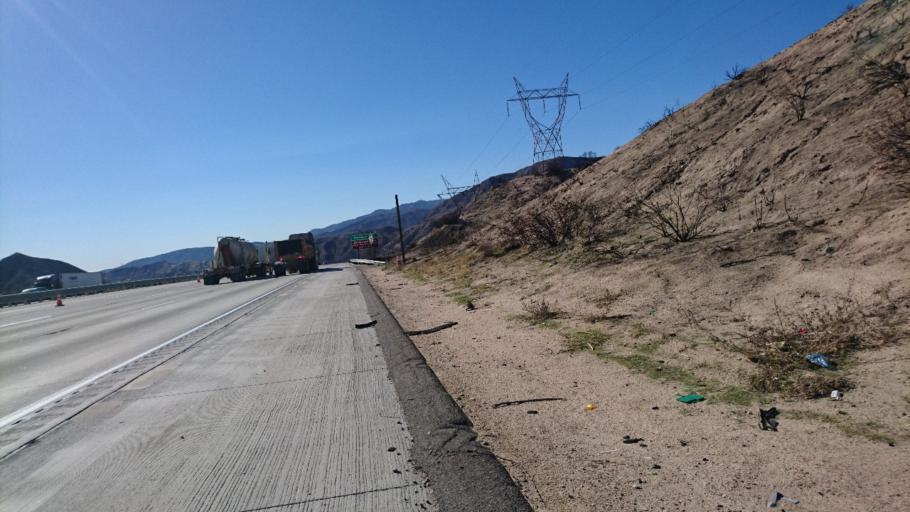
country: US
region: California
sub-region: San Bernardino County
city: Oak Hills
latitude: 34.3310
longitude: -117.4826
